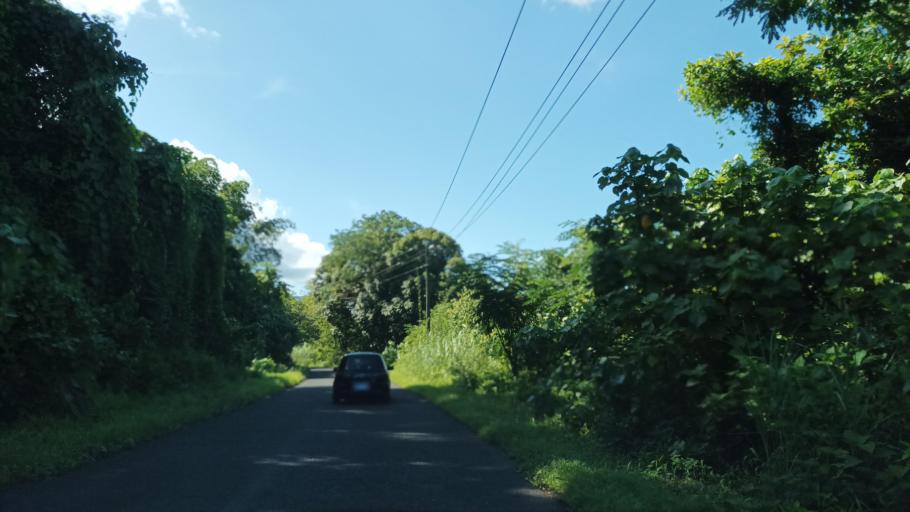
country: FM
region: Pohnpei
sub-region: Madolenihm Municipality
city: Madolenihm Municipality Government
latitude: 6.8616
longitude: 158.2937
